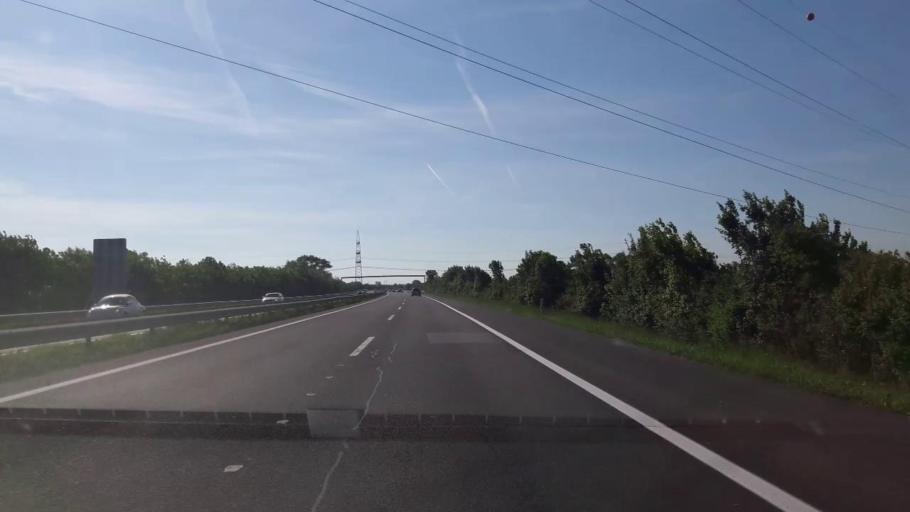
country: AT
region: Lower Austria
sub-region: Politischer Bezirk Modling
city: Munchendorf
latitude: 48.0105
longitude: 16.3713
